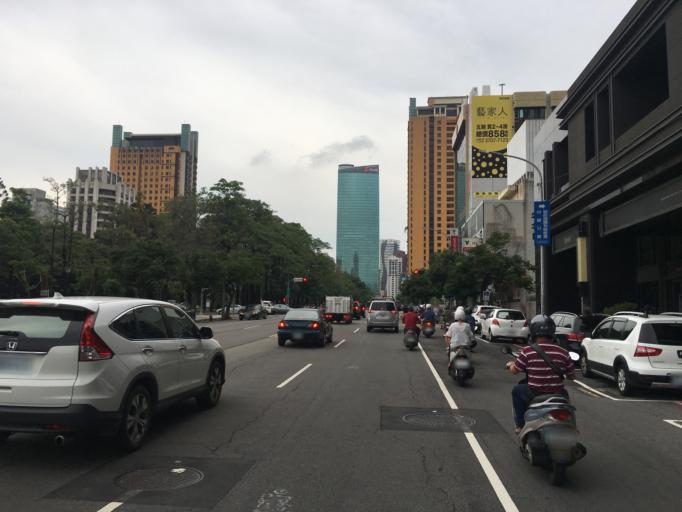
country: TW
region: Taiwan
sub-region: Taichung City
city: Taichung
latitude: 24.1435
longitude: 120.6653
